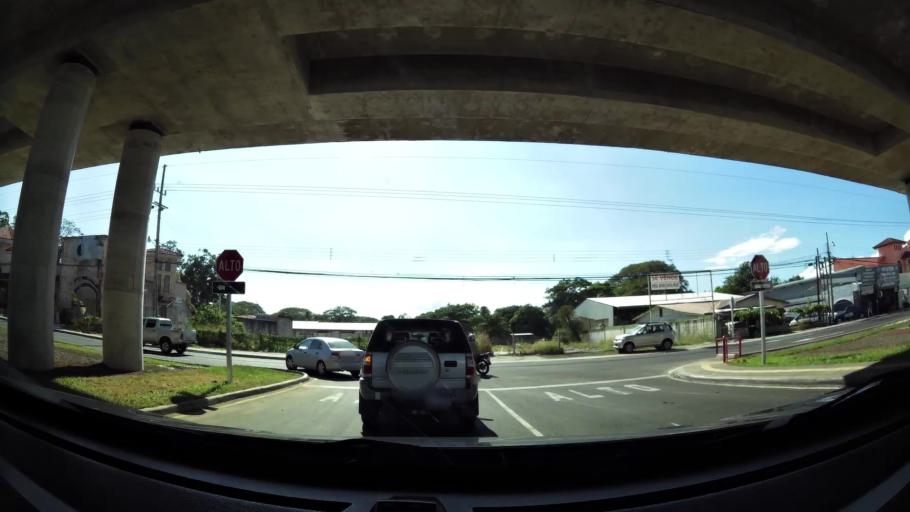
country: CR
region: Guanacaste
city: Liberia
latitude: 10.6274
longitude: -85.4441
